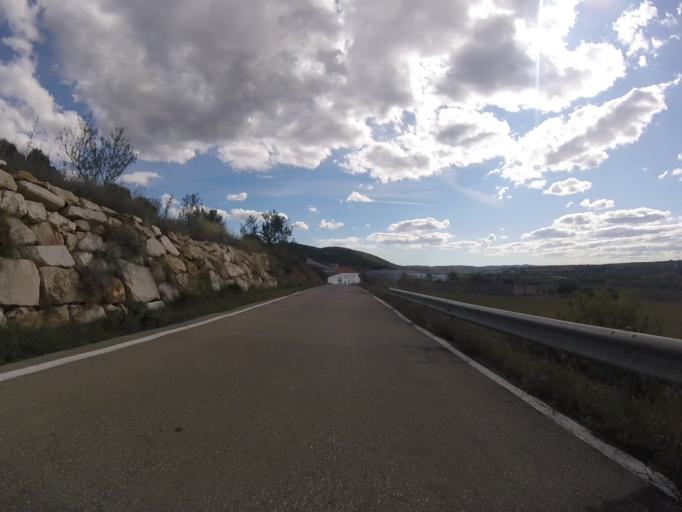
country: ES
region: Valencia
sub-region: Provincia de Castello
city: Cuevas de Vinroma
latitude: 40.3518
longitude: 0.1279
